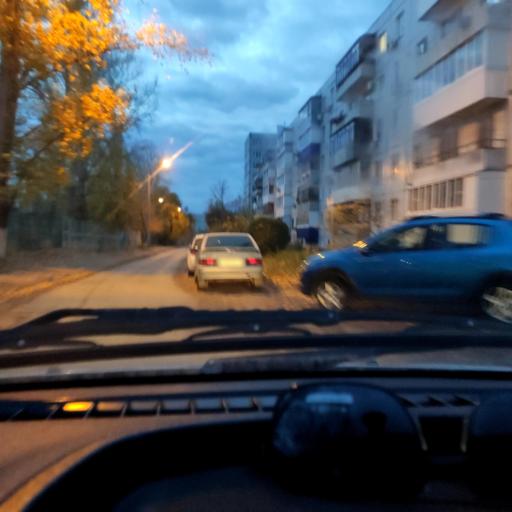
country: RU
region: Samara
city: Zhigulevsk
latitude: 53.4797
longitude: 49.4814
